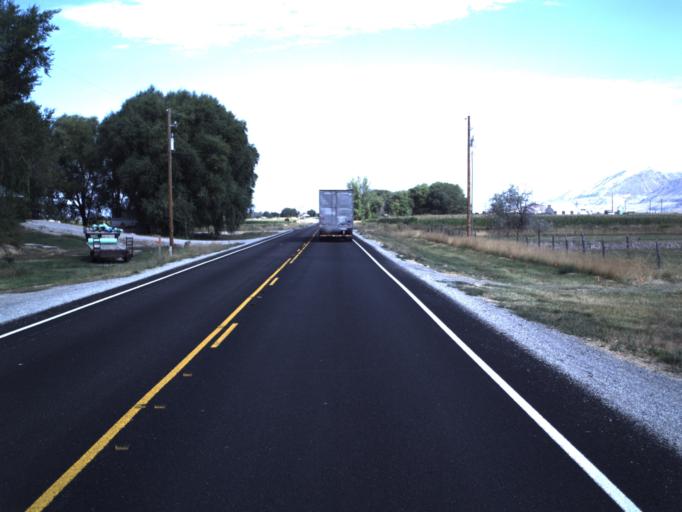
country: US
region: Utah
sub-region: Box Elder County
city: Honeyville
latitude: 41.6215
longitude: -112.1268
